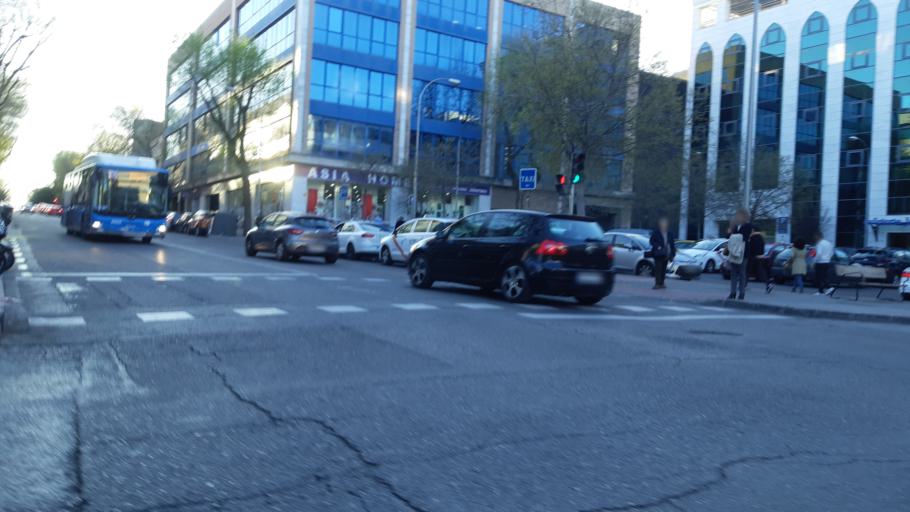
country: ES
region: Madrid
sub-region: Provincia de Madrid
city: San Blas
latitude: 40.4340
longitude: -3.6320
